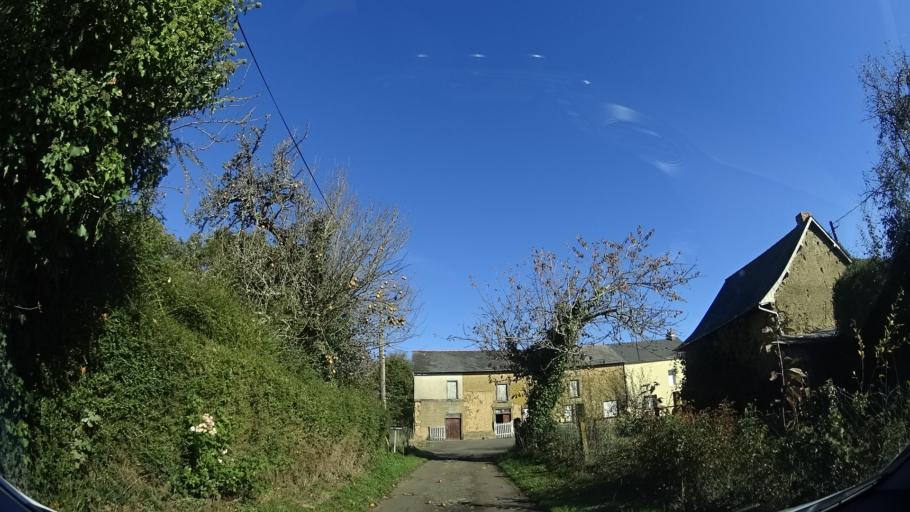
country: FR
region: Brittany
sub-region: Departement d'Ille-et-Vilaine
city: Geveze
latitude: 48.2186
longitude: -1.7730
